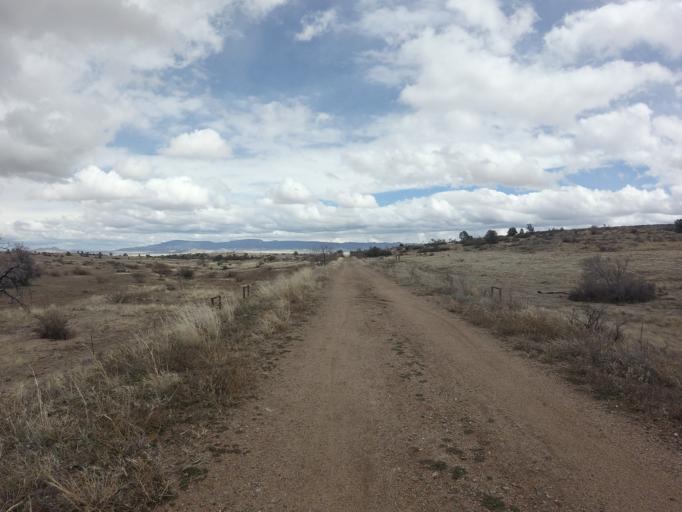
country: US
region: Arizona
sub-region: Yavapai County
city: Prescott Valley
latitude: 34.6102
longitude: -112.3857
